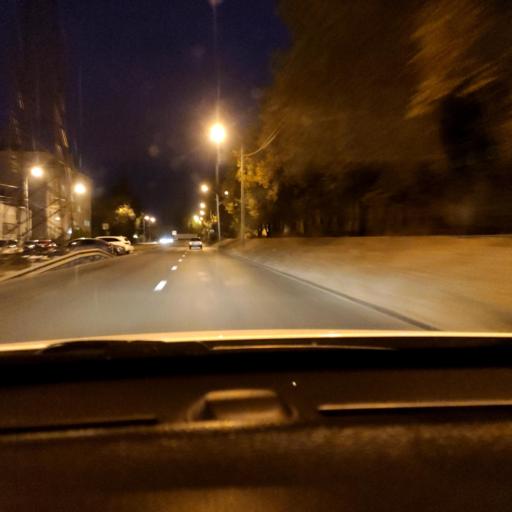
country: RU
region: Voronezj
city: Voronezh
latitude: 51.6896
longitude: 39.1610
